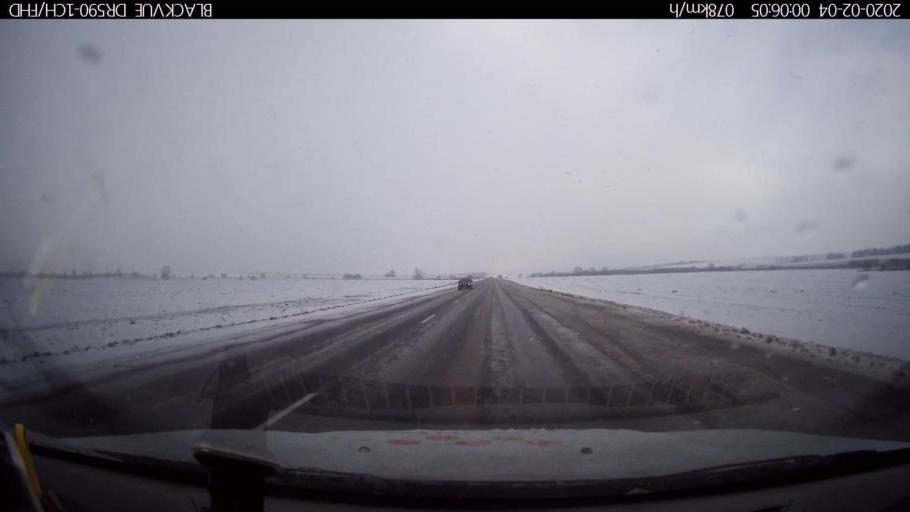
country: RU
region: Nizjnij Novgorod
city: Dal'neye Konstantinovo
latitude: 55.8439
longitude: 44.1269
